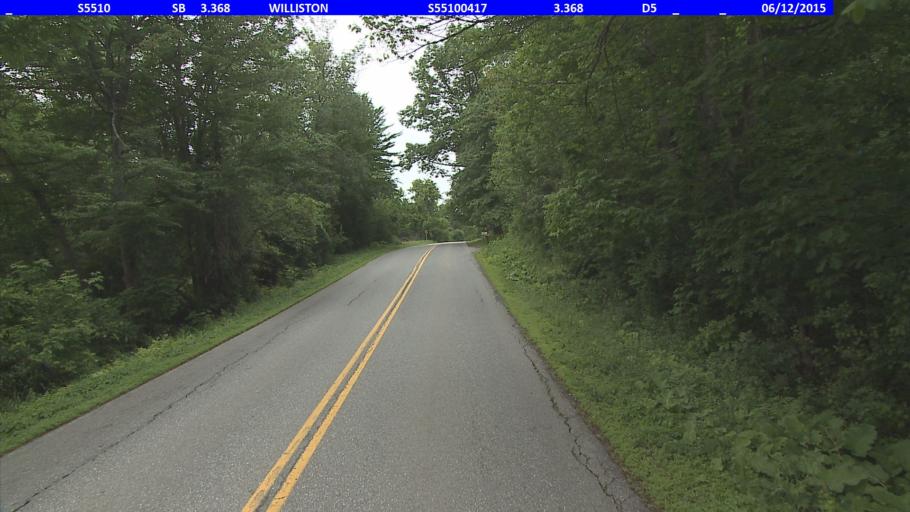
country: US
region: Vermont
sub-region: Chittenden County
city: Williston
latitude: 44.4187
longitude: -73.0826
